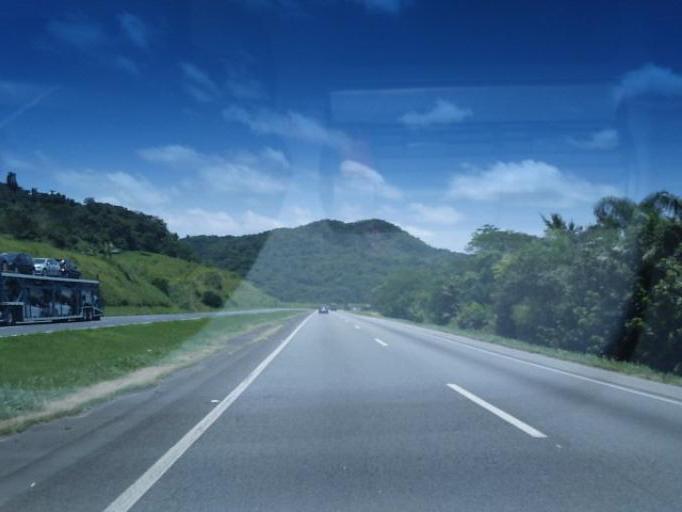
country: BR
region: Sao Paulo
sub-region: Juquia
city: Juquia
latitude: -24.3539
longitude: -47.6603
